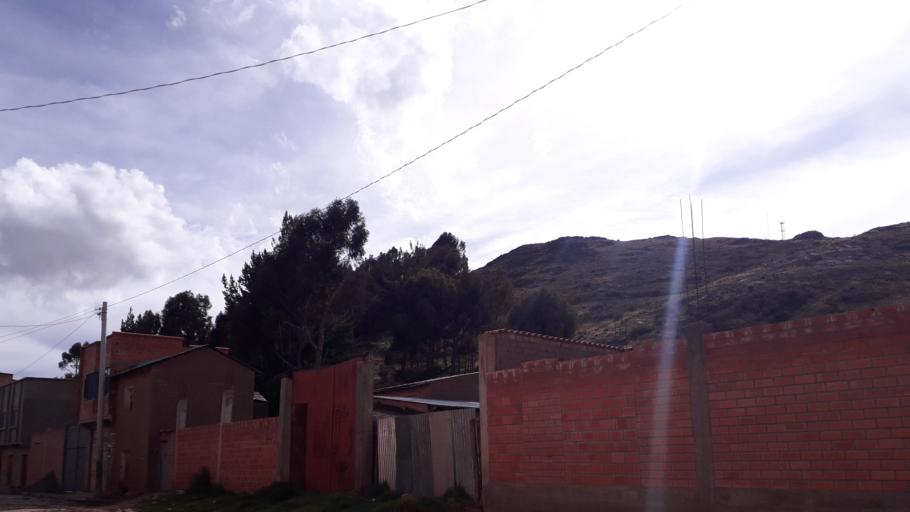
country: PE
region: Puno
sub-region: Moho
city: Putina
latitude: -15.5349
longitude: -69.2534
